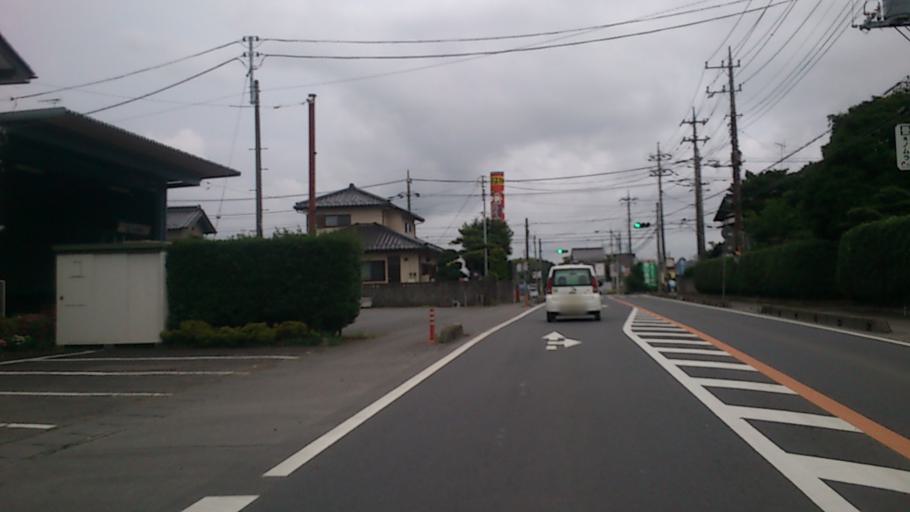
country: JP
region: Ibaraki
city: Ishige
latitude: 36.1151
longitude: 139.9375
